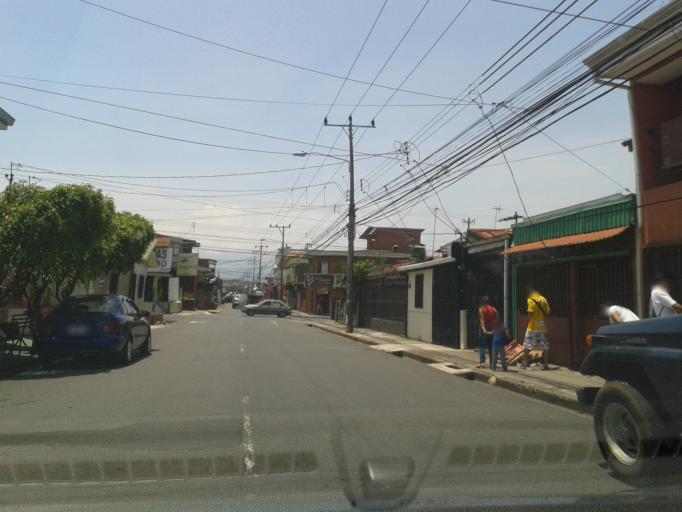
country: CR
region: Heredia
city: San Francisco
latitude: 9.9944
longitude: -84.1232
